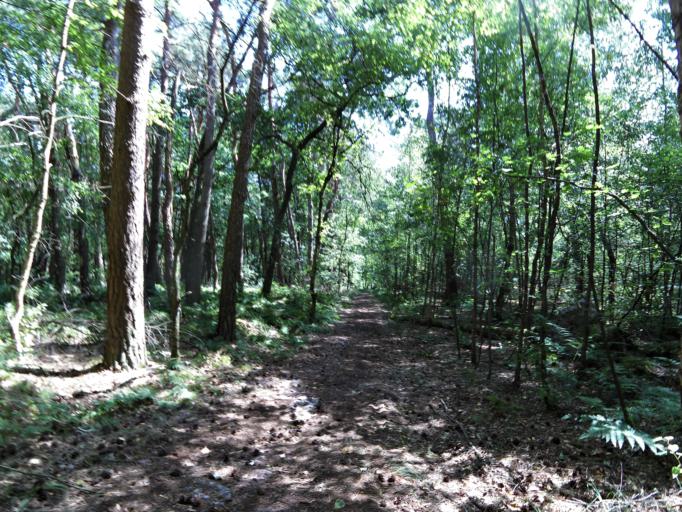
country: NL
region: Limburg
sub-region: Gemeente Leudal
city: Heythuysen
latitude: 51.2100
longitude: 5.8975
